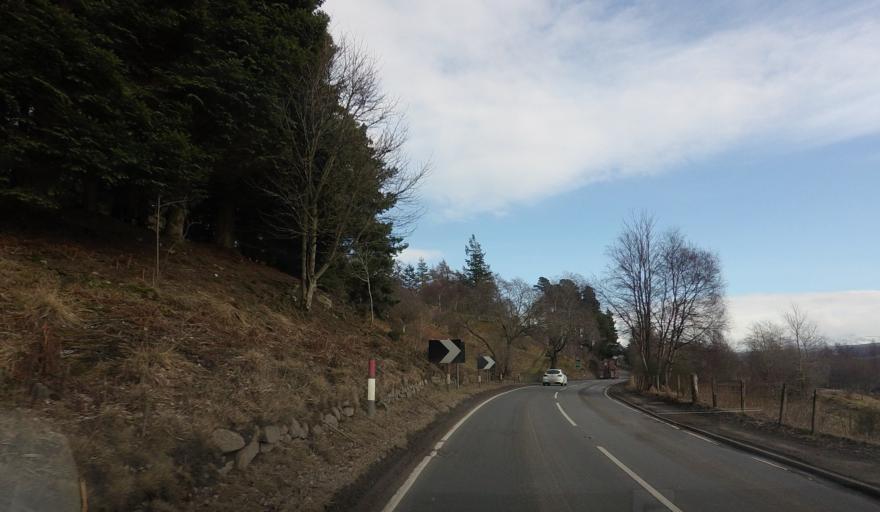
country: GB
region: Scotland
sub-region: Highland
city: Kingussie
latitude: 57.0778
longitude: -4.0671
